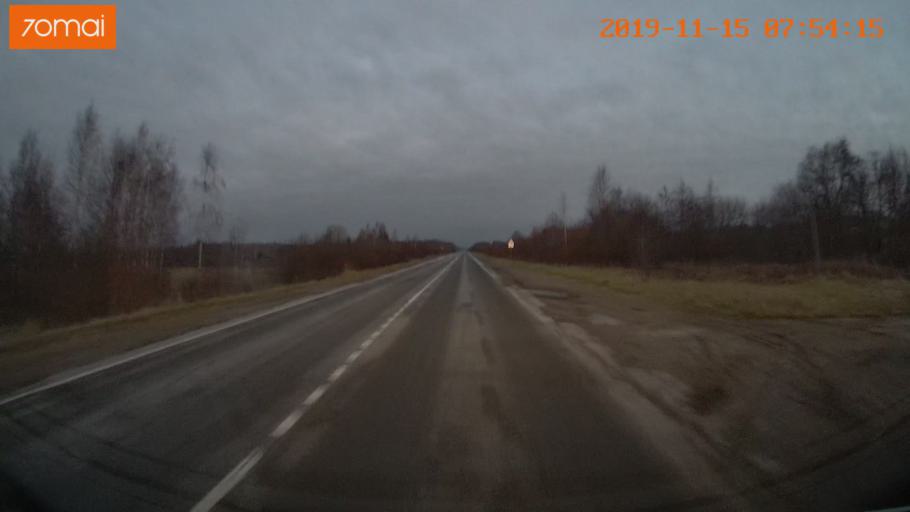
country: RU
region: Vologda
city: Cherepovets
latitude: 58.8968
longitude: 38.1780
